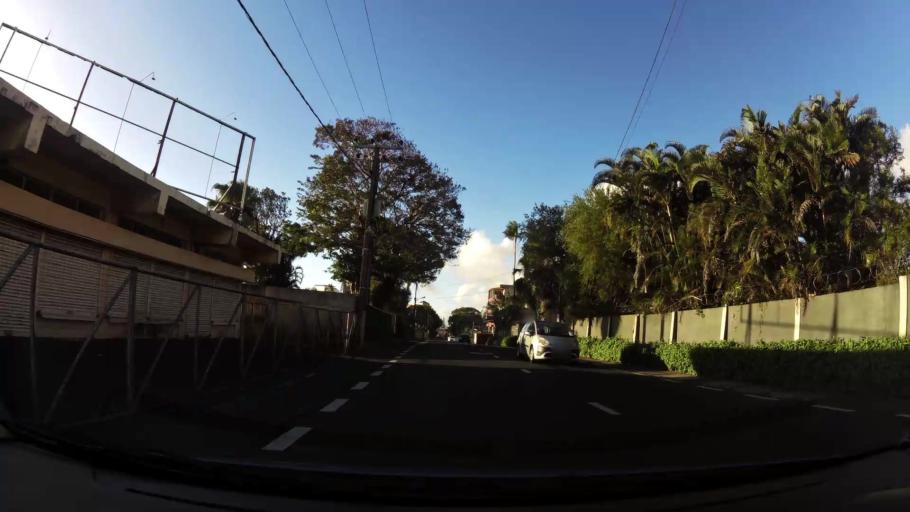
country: MU
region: Plaines Wilhems
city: Curepipe
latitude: -20.3098
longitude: 57.5246
